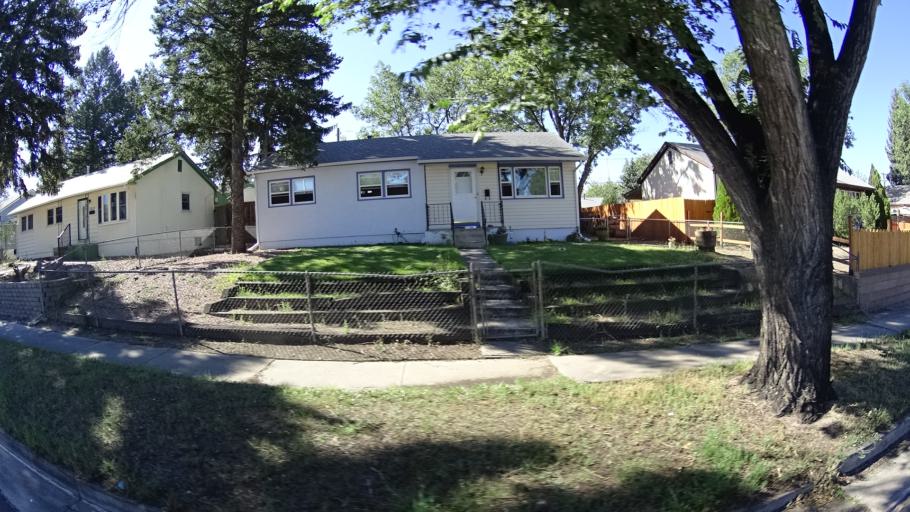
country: US
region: Colorado
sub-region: El Paso County
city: Colorado Springs
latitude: 38.8544
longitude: -104.7728
